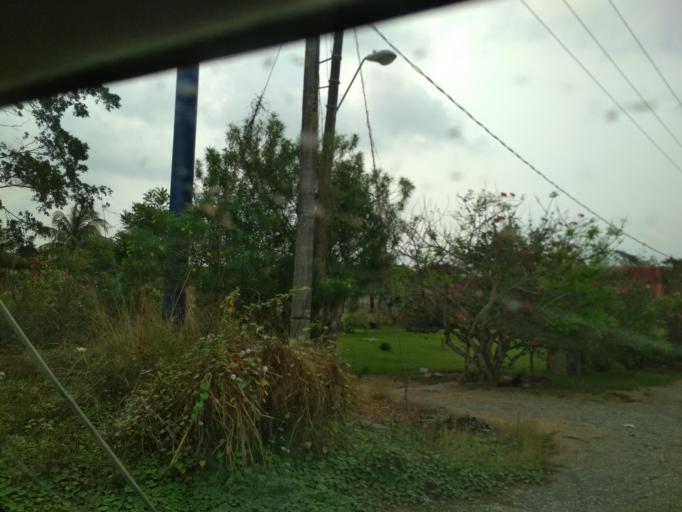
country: MX
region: Veracruz
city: Paso del Toro
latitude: 19.0090
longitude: -96.1164
